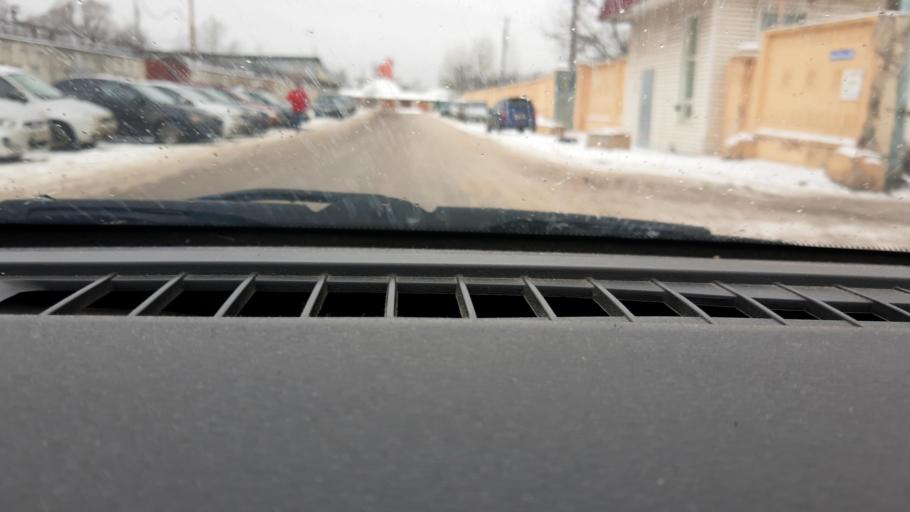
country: RU
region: Nizjnij Novgorod
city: Gorbatovka
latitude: 56.3365
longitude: 43.8082
